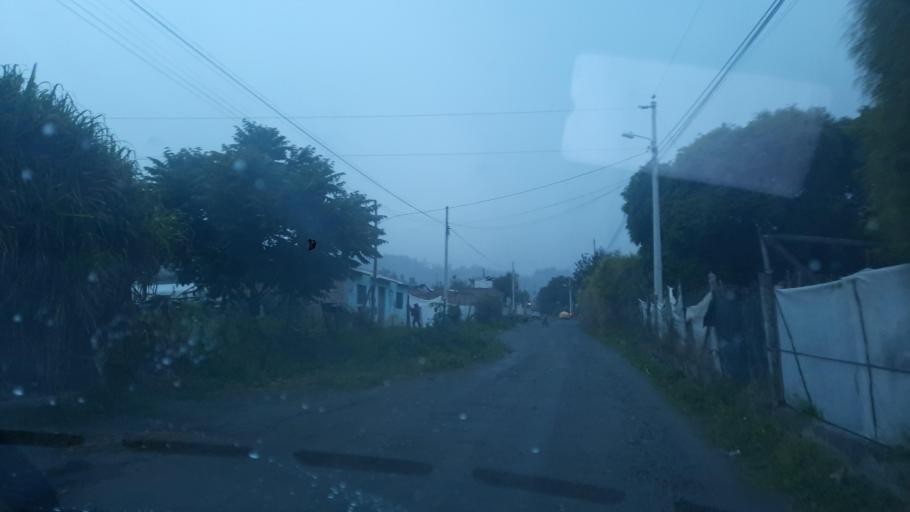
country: EC
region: Chimborazo
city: Riobamba
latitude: -1.6863
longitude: -78.6669
